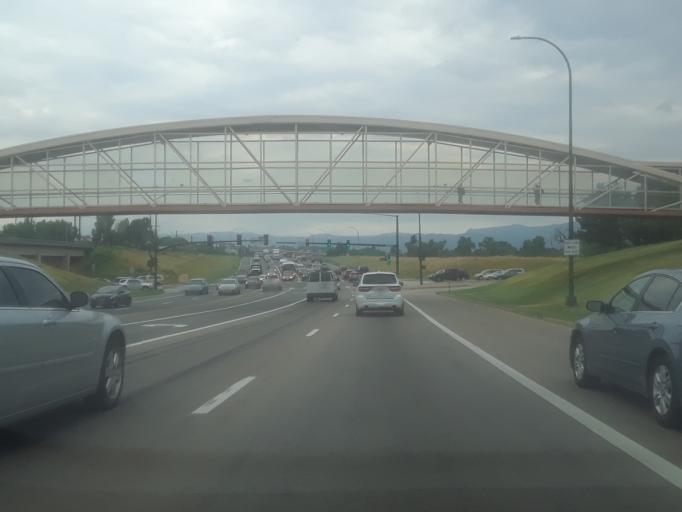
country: US
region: Colorado
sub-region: Arapahoe County
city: Columbine Valley
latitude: 39.5805
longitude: -105.0254
